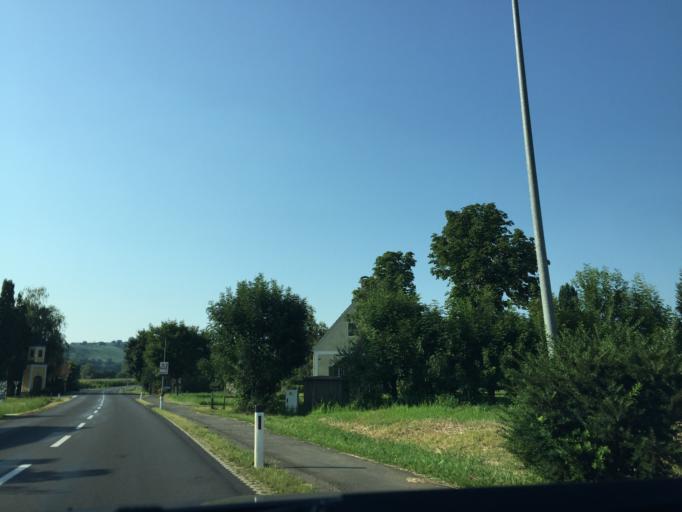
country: AT
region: Styria
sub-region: Politischer Bezirk Suedoststeiermark
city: Straden
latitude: 46.7794
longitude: 15.8581
